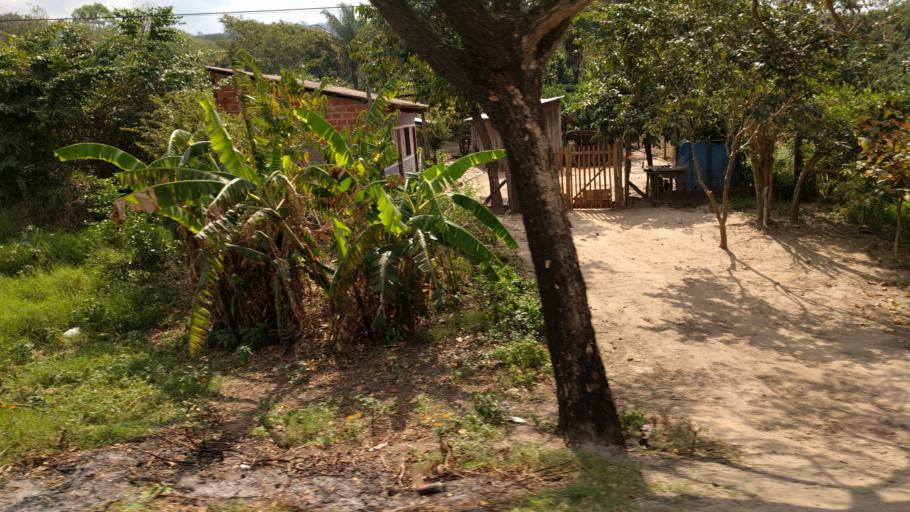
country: BO
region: Santa Cruz
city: Jorochito
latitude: -18.1523
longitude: -63.4928
